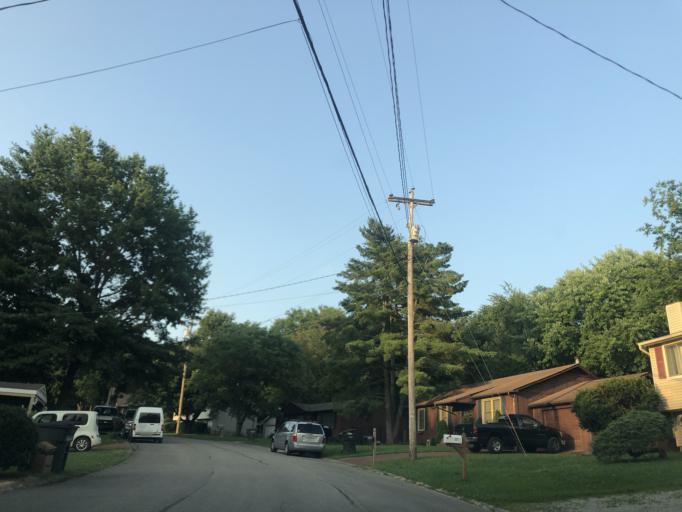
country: US
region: Tennessee
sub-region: Davidson County
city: Lakewood
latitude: 36.1402
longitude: -86.6343
